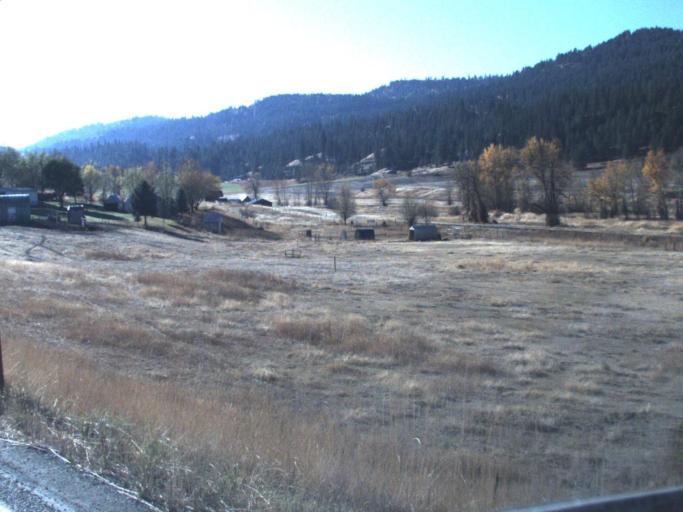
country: CA
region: British Columbia
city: Grand Forks
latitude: 48.8676
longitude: -118.6061
